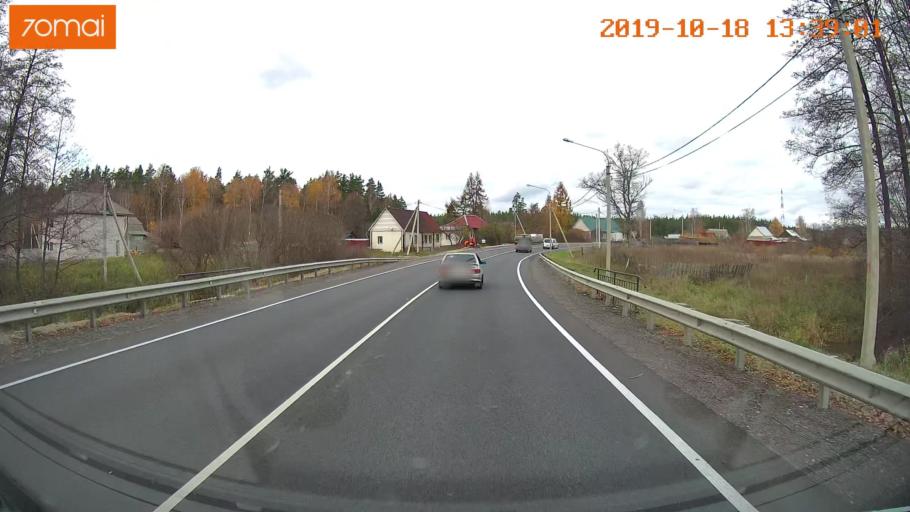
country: RU
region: Rjazan
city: Solotcha
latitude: 54.8945
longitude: 40.0004
